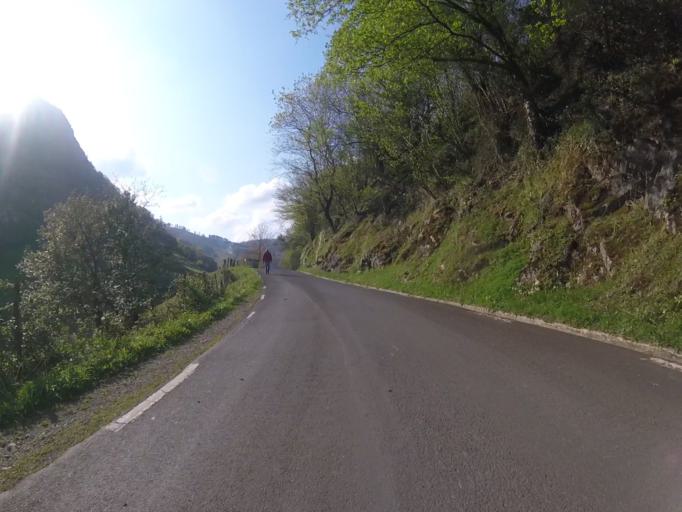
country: ES
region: Basque Country
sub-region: Provincia de Guipuzcoa
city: Azkoitia
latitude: 43.2357
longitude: -2.3242
